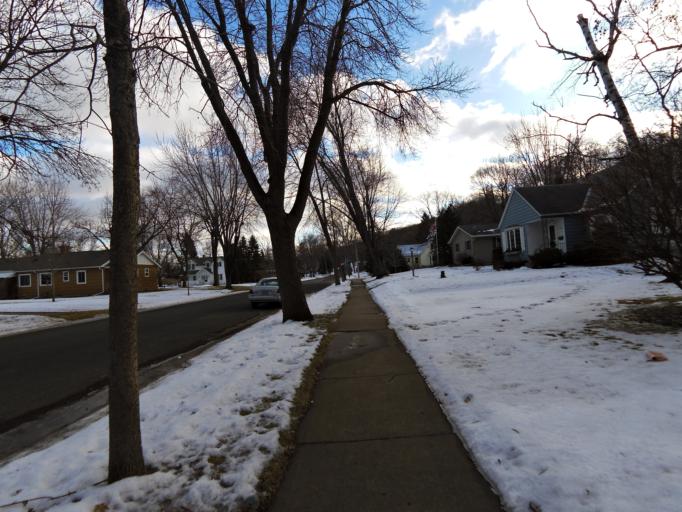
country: US
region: Minnesota
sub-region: Washington County
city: Bayport
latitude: 45.0158
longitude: -92.7825
